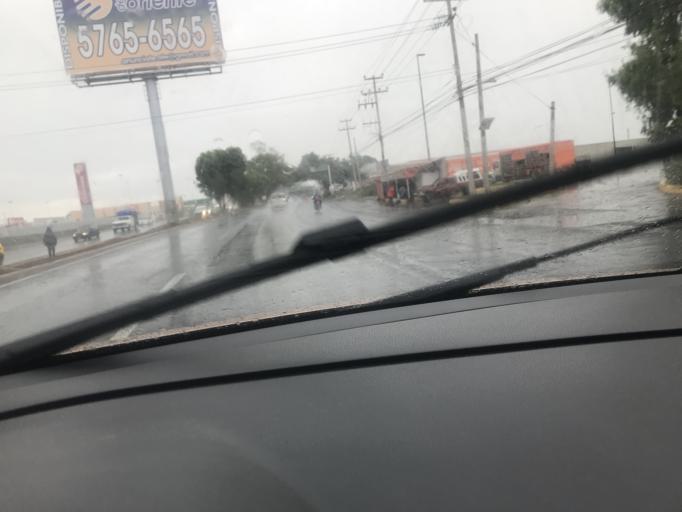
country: MX
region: Mexico
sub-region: Texcoco
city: Santa Martha
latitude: 19.4238
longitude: -98.9124
